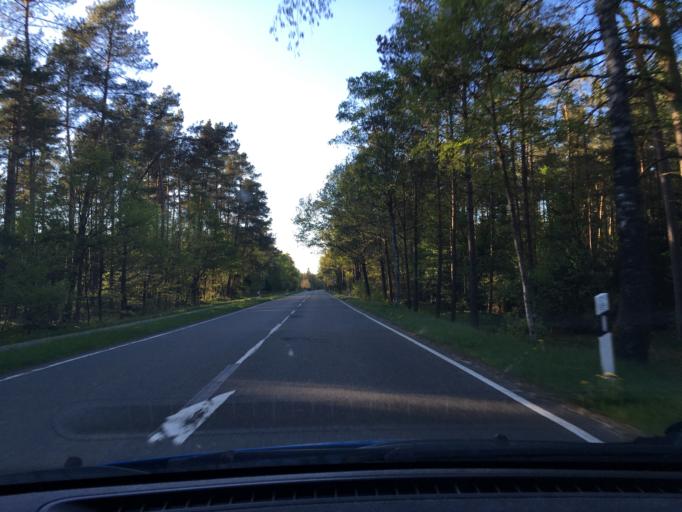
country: DE
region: Lower Saxony
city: Bispingen
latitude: 53.0375
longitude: 9.9960
